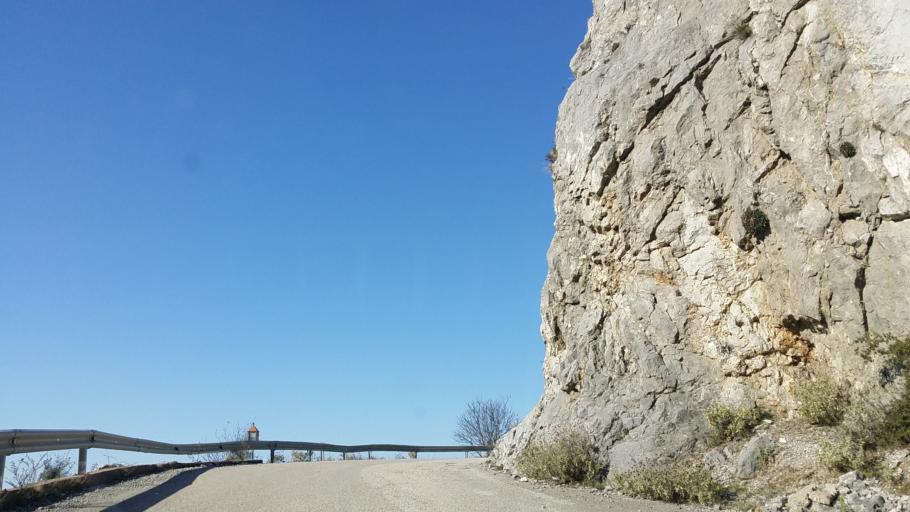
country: GR
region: West Greece
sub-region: Nomos Aitolias kai Akarnanias
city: Sardinia
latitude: 38.9257
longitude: 21.4058
